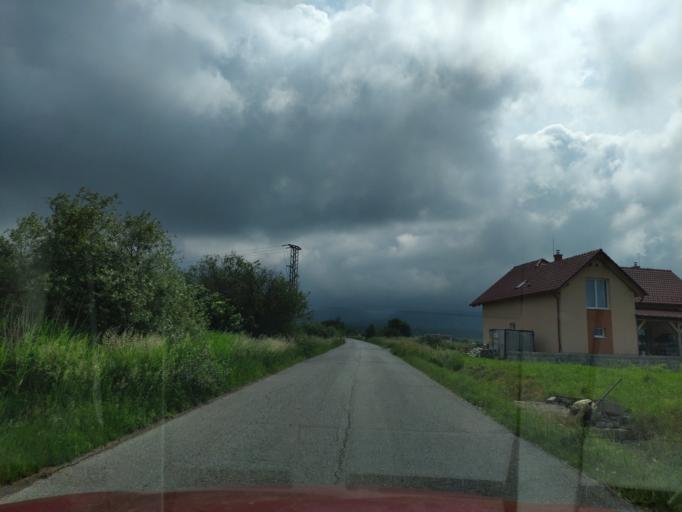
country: SK
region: Presovsky
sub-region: Okres Presov
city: Presov
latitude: 48.9971
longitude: 21.2922
